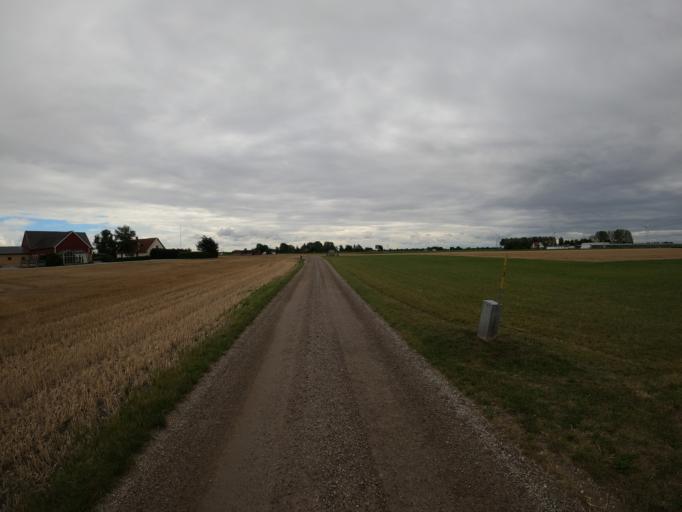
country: SE
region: Skane
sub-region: Kavlinge Kommun
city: Kaevlinge
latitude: 55.7516
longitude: 13.1285
